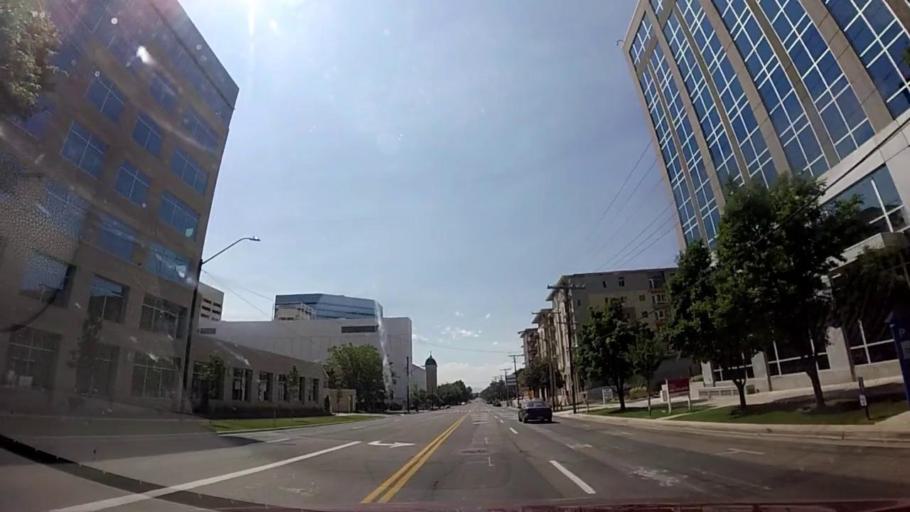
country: US
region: Utah
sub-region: Salt Lake County
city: Salt Lake City
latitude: 40.7667
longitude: -111.8854
